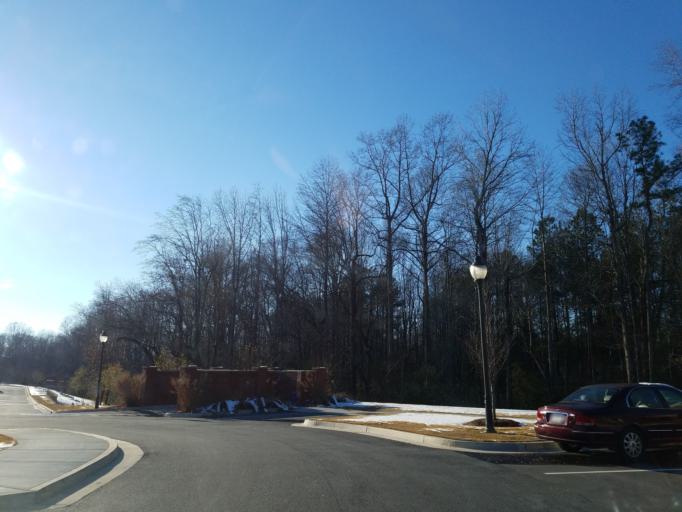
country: US
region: Georgia
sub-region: Dawson County
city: Dawsonville
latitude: 34.3584
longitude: -84.0332
